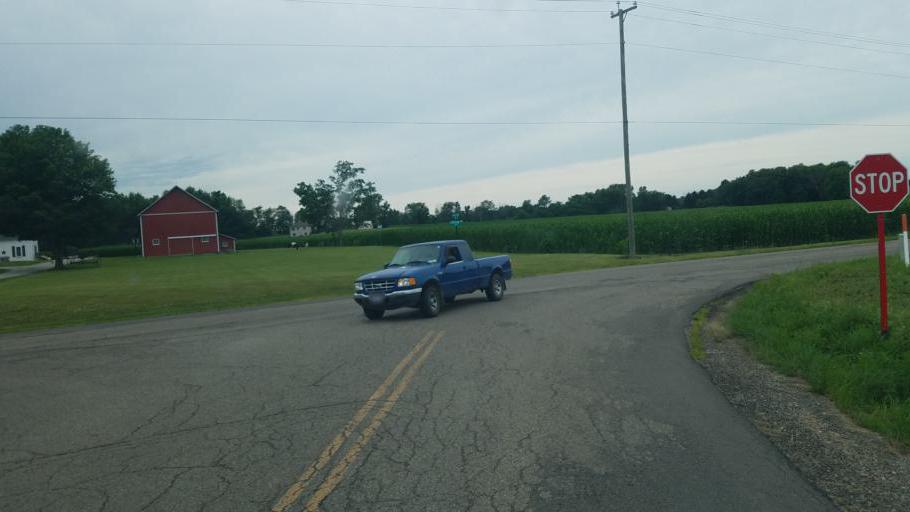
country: US
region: Ohio
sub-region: Knox County
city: Centerburg
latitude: 40.2790
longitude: -82.6896
